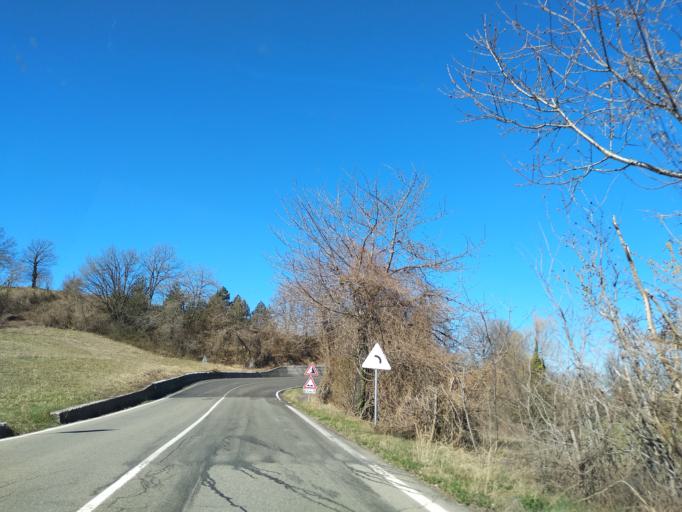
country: IT
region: Emilia-Romagna
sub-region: Provincia di Reggio Emilia
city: Castelnovo ne'Monti
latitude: 44.4161
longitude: 10.3527
